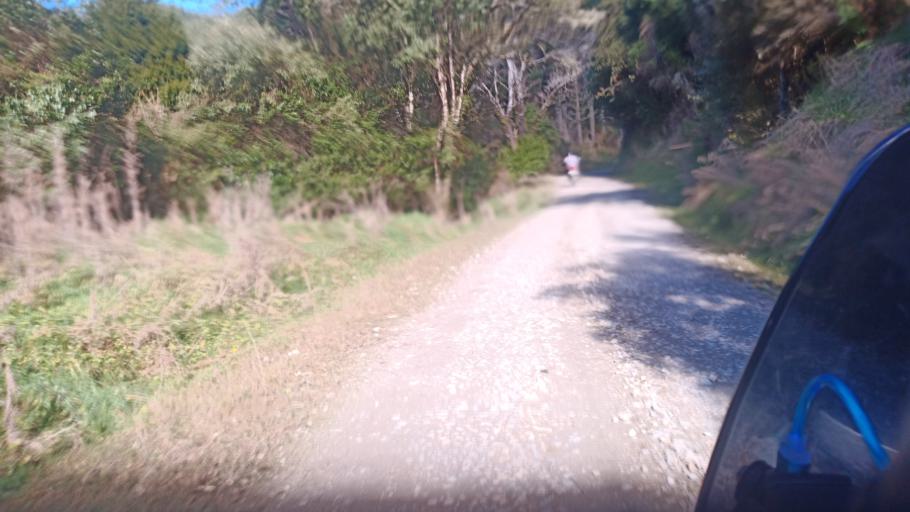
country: NZ
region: Hawke's Bay
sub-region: Wairoa District
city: Wairoa
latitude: -38.6646
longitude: 177.5150
